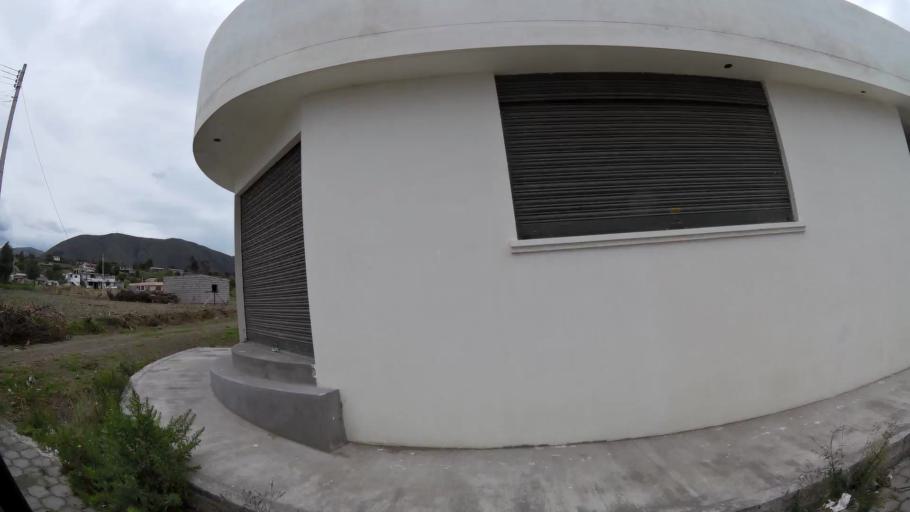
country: EC
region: Cotopaxi
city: Latacunga
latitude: -0.9548
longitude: -78.6022
